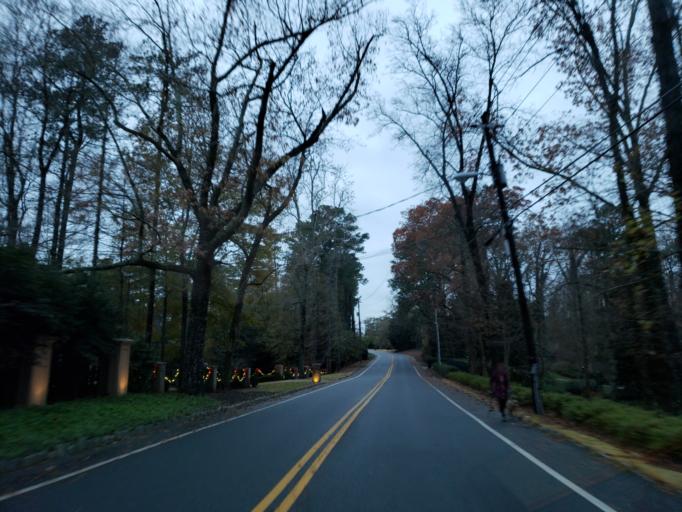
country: US
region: Georgia
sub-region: Cobb County
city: Vinings
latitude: 33.8811
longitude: -84.4203
